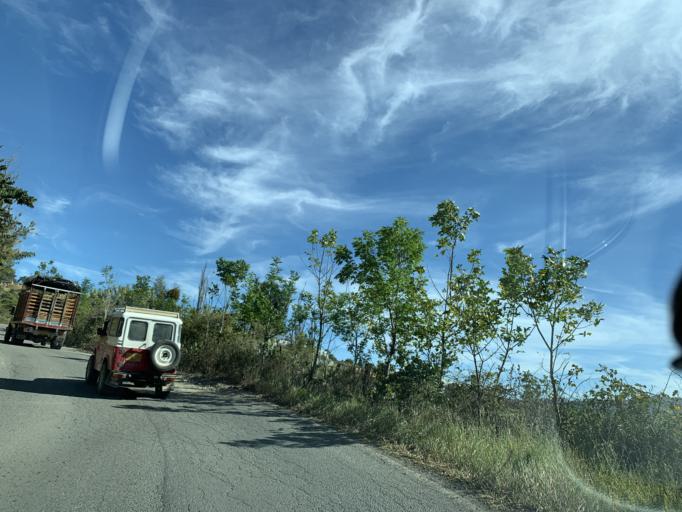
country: CO
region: Boyaca
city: Villa de Leiva
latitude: 5.6724
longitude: -73.5857
